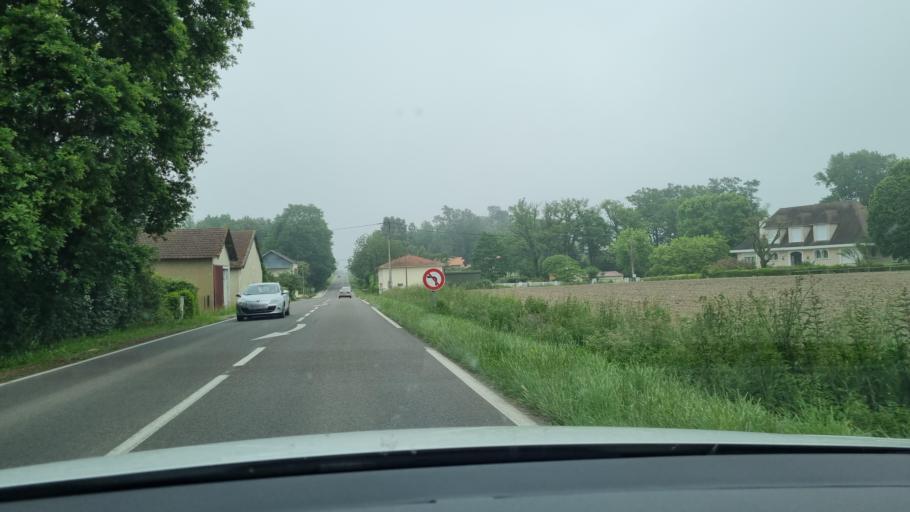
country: FR
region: Aquitaine
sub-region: Departement des Landes
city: Hagetmau
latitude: 43.6413
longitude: -0.6105
